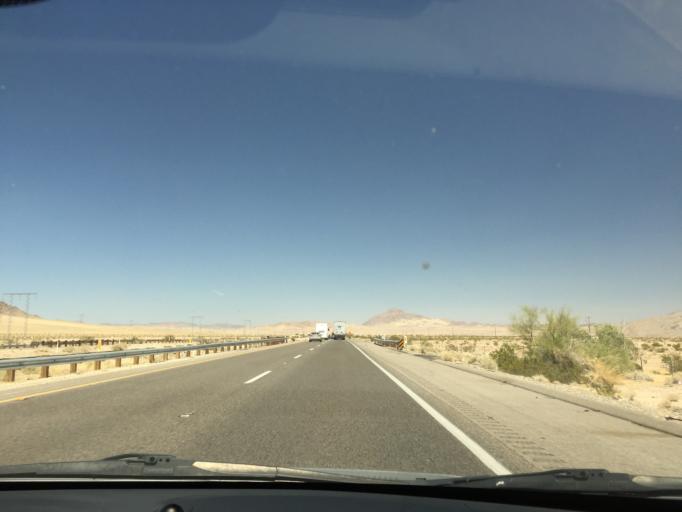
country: US
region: California
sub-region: San Bernardino County
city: Fort Irwin
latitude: 35.0265
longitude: -116.4874
